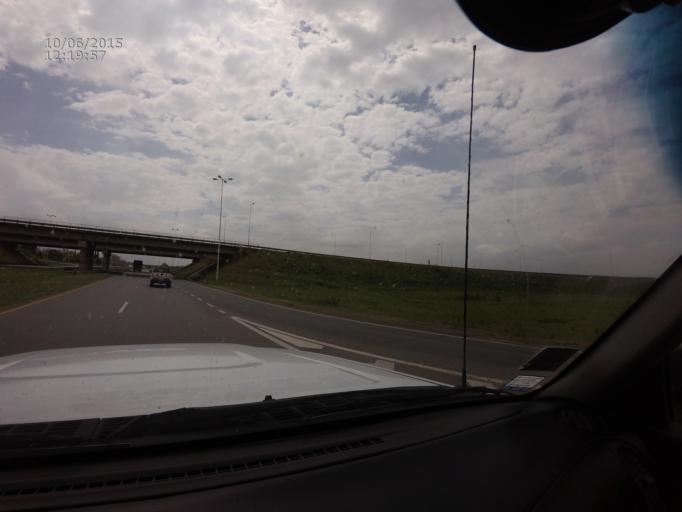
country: AR
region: Santa Fe
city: Roldan
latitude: -32.9274
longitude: -60.8999
